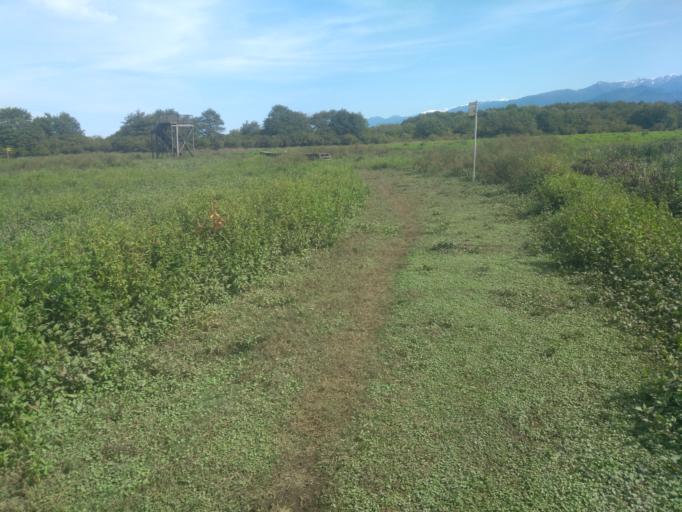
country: GE
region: Ajaria
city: Kobuleti
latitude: 41.8634
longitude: 41.7890
